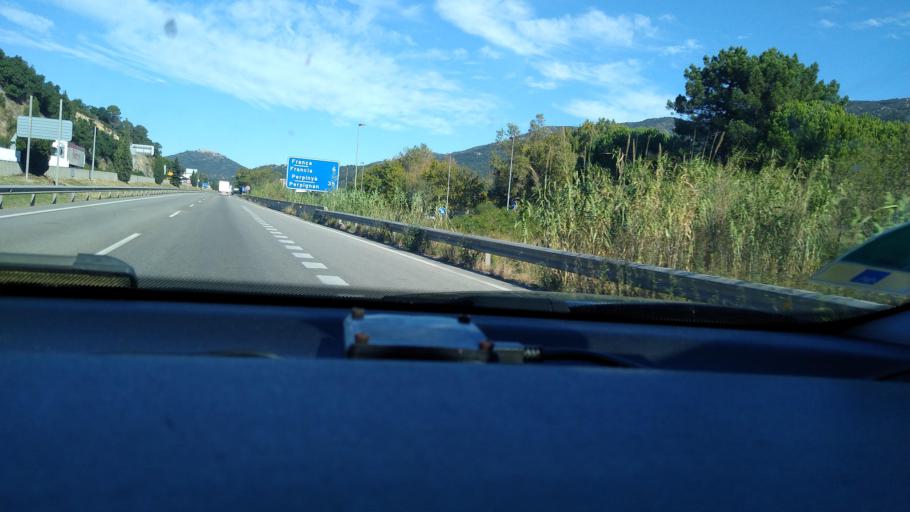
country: ES
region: Catalonia
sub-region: Provincia de Girona
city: la Jonquera
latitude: 42.4138
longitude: 2.8722
